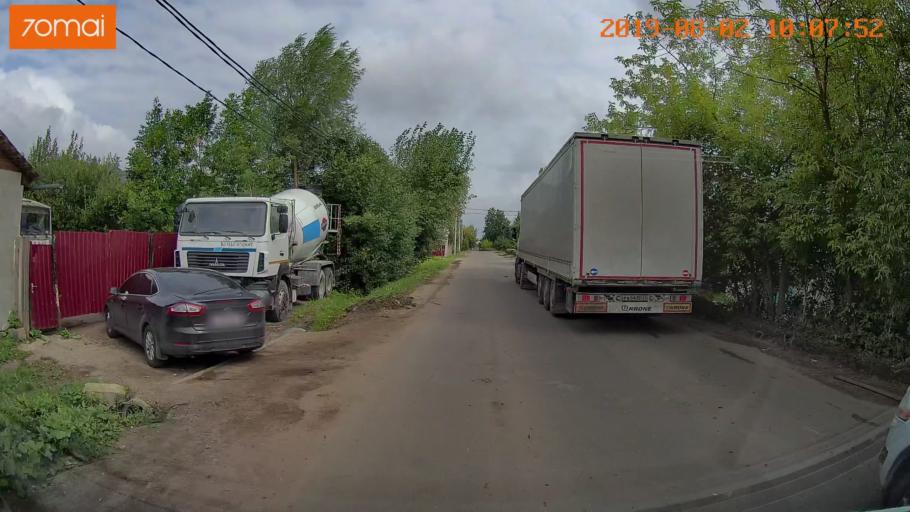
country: RU
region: Ivanovo
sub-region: Gorod Ivanovo
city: Ivanovo
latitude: 56.9838
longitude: 40.9365
